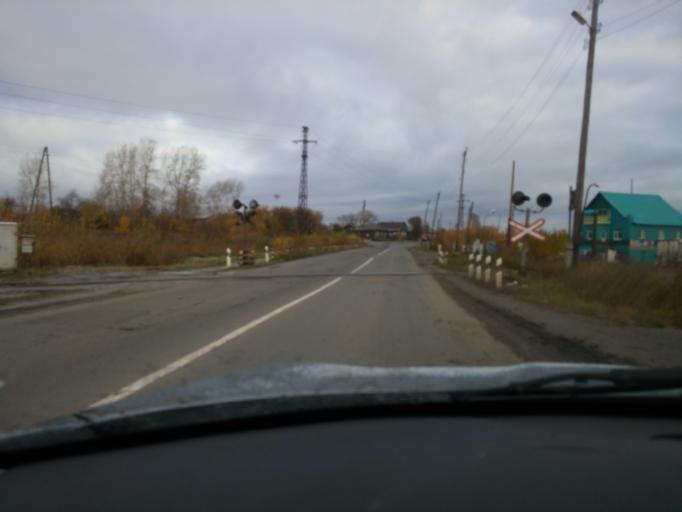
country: RU
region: Sverdlovsk
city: Turinsk
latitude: 58.0305
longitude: 63.7026
